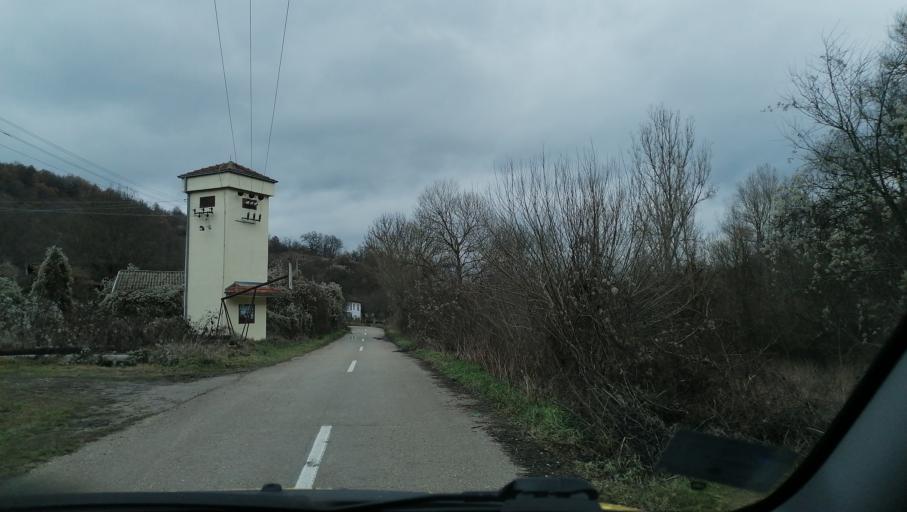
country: RS
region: Central Serbia
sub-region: Pirotski Okrug
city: Dimitrovgrad
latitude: 42.9278
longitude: 22.7602
